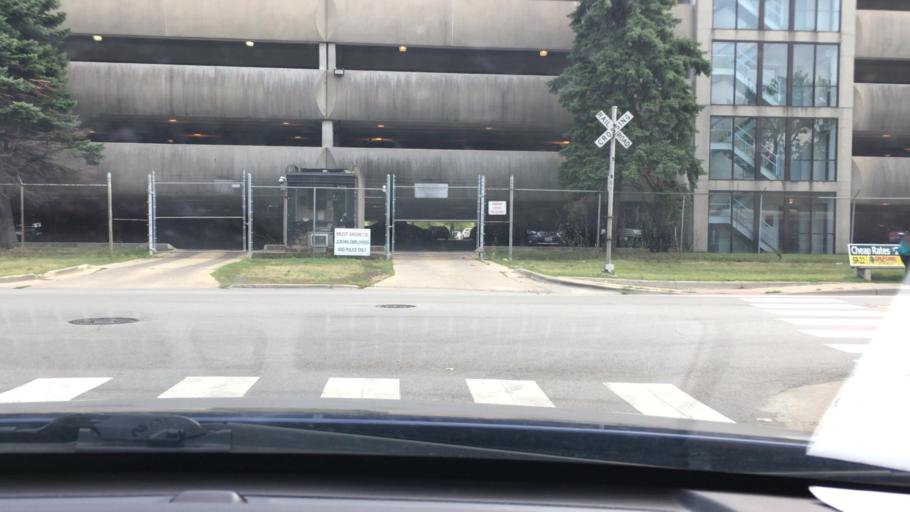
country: US
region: Illinois
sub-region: Cook County
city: Chicago
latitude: 41.8449
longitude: -87.6928
